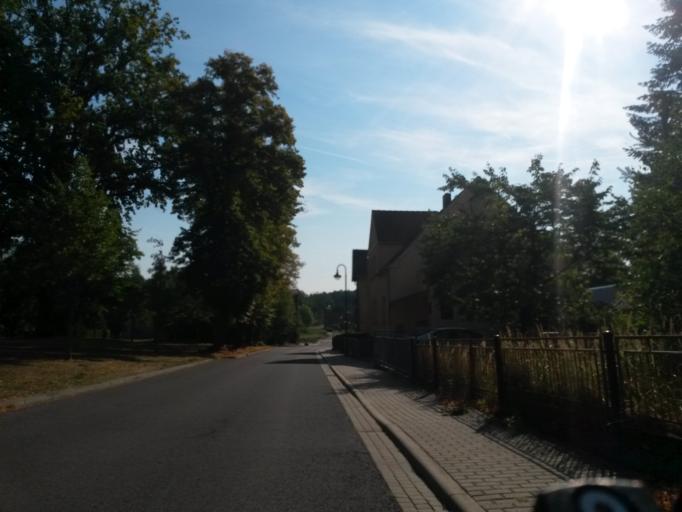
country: DE
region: Saxony-Anhalt
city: Nudersdorf
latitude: 51.9301
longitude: 12.5970
